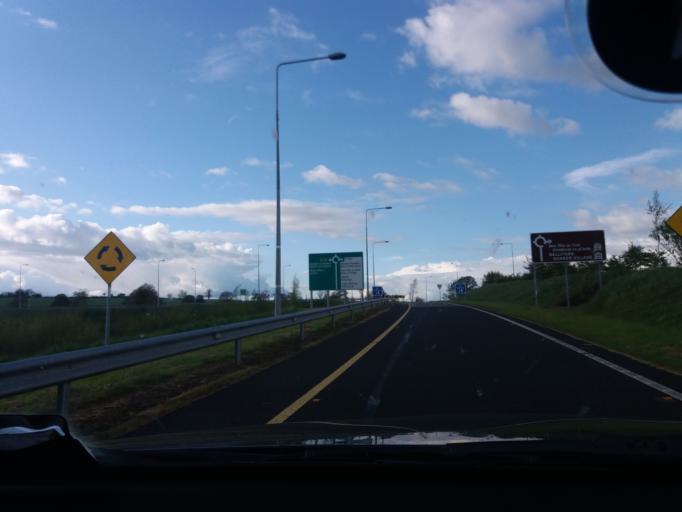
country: IE
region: Leinster
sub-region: Kildare
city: Moone
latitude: 52.9974
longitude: -6.8439
